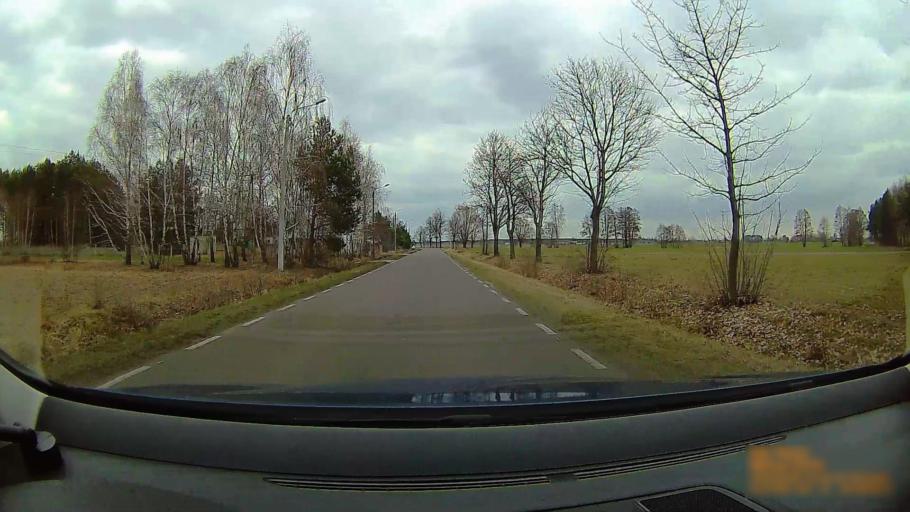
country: PL
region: Greater Poland Voivodeship
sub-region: Powiat koninski
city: Rzgow Pierwszy
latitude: 52.1019
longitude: 18.0959
